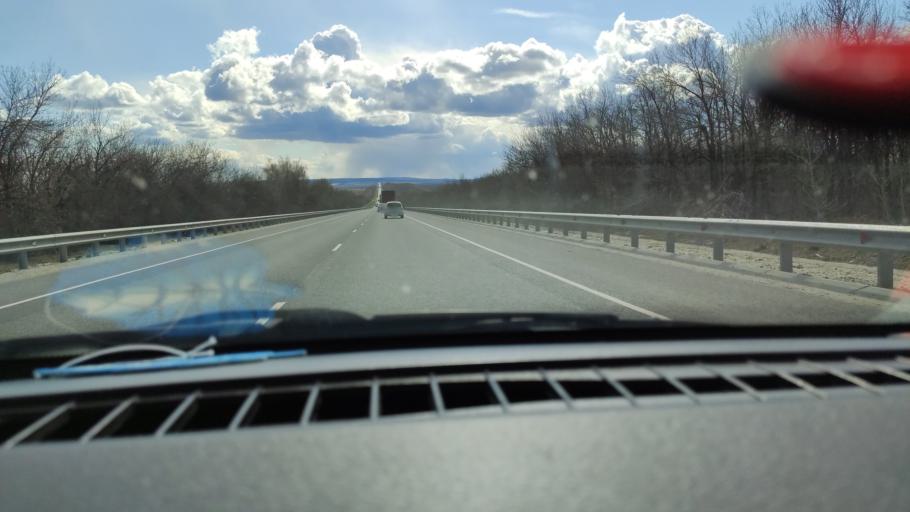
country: RU
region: Saratov
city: Khvalynsk
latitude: 52.6157
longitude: 48.1657
